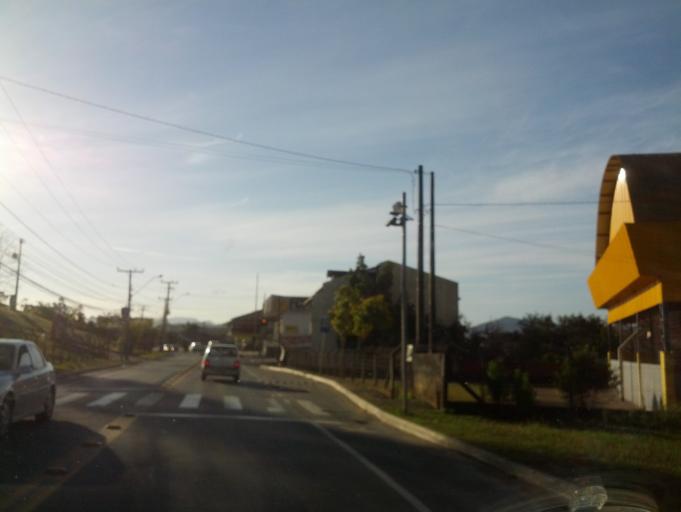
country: BR
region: Santa Catarina
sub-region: Indaial
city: Indaial
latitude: -26.8874
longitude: -49.2169
